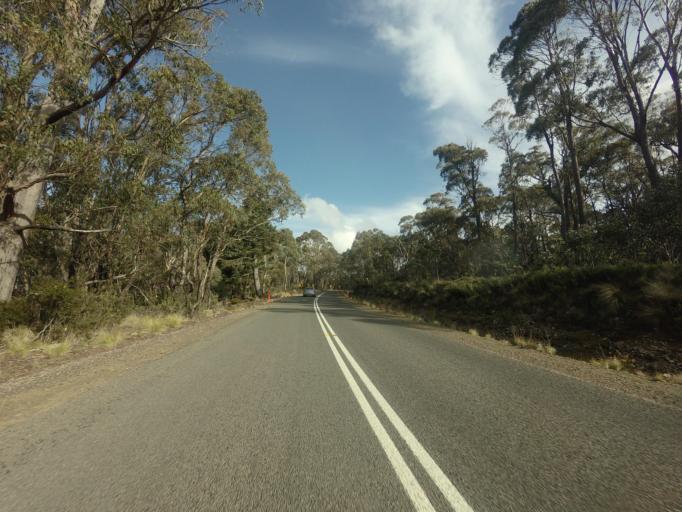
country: AU
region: Tasmania
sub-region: Meander Valley
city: Deloraine
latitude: -41.7854
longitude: 146.7036
